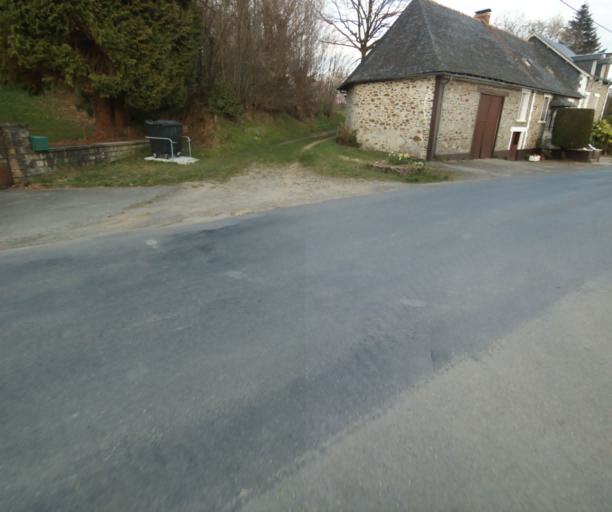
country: FR
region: Limousin
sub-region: Departement de la Correze
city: Saint-Clement
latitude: 45.3608
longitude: 1.6273
